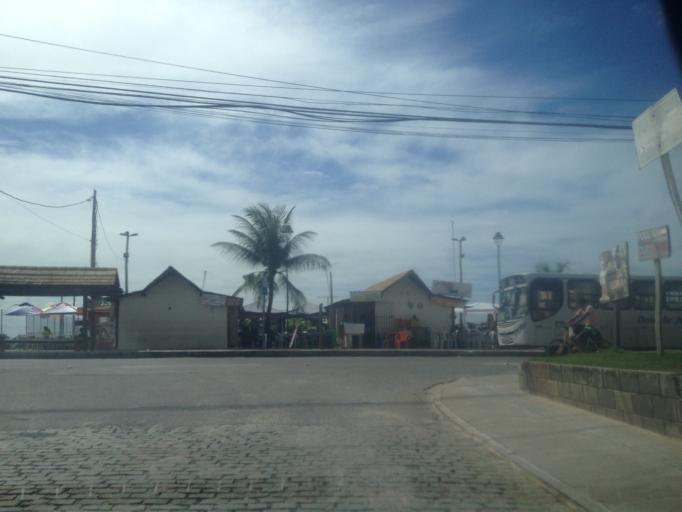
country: BR
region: Bahia
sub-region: Camacari
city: Camacari
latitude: -12.7717
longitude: -38.1779
